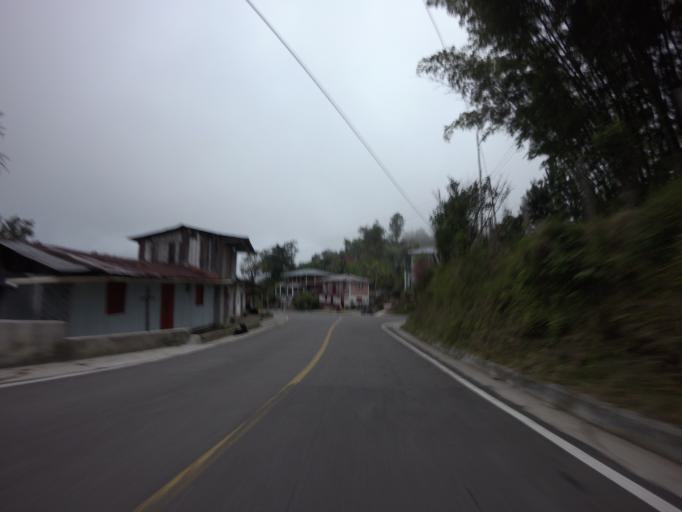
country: CO
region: Caldas
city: Manzanares
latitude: 5.3155
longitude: -75.1312
